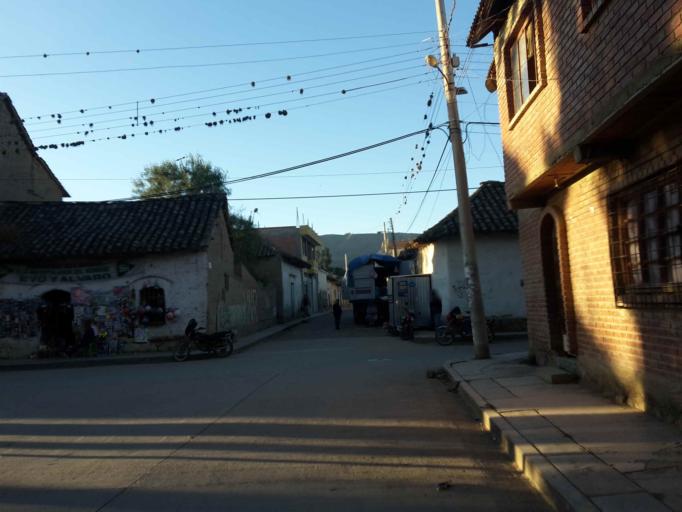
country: BO
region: Cochabamba
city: Capinota
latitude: -17.5501
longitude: -66.2480
